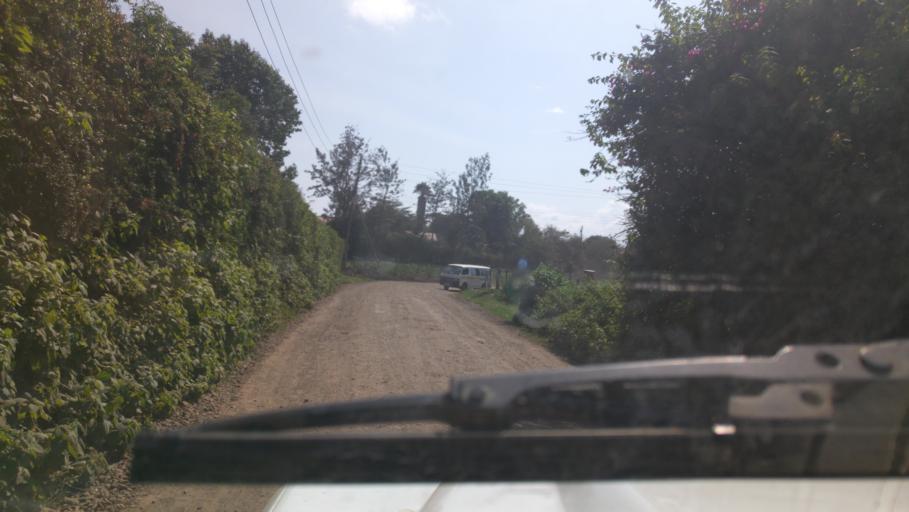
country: KE
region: Nakuru
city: Nakuru
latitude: -0.2767
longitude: 36.1052
